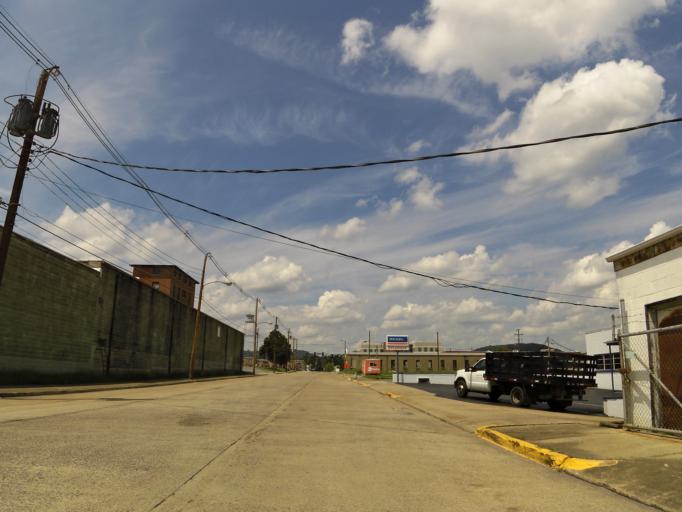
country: US
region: Tennessee
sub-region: Sullivan County
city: Kingsport
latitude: 36.5511
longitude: -82.5622
